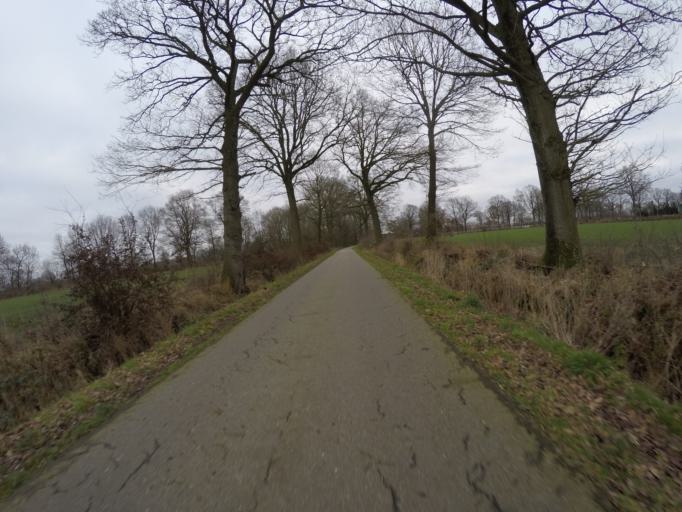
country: DE
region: Schleswig-Holstein
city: Bilsen
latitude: 53.7973
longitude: 9.8817
